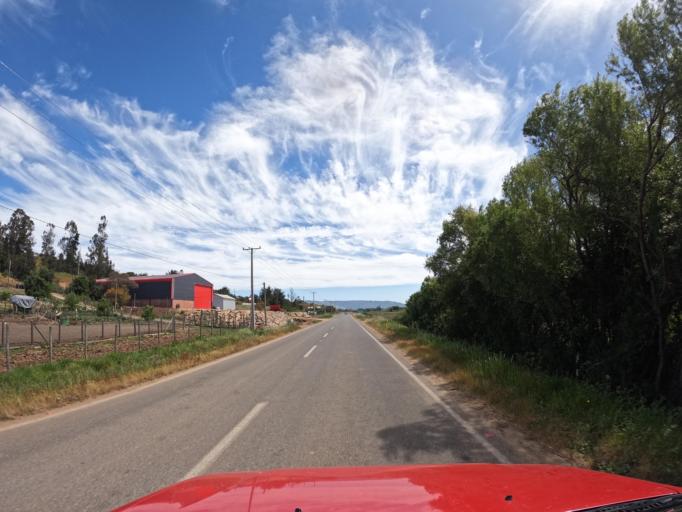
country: CL
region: Maule
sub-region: Provincia de Talca
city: Constitucion
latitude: -34.9972
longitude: -72.0222
